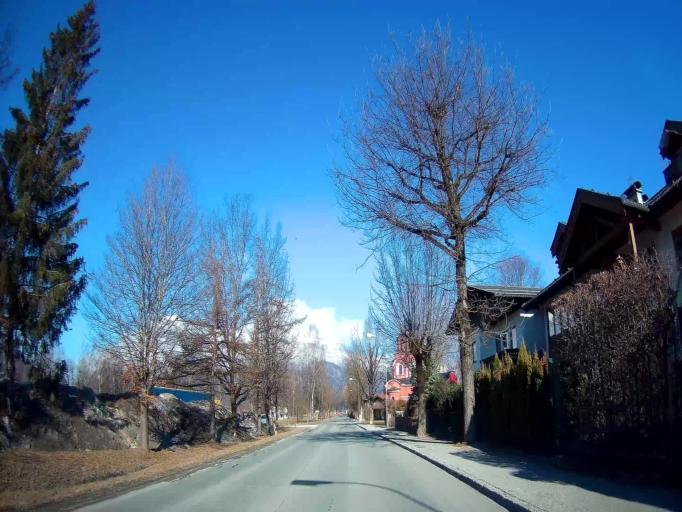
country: AT
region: Salzburg
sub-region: Politischer Bezirk Zell am See
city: Saalfelden am Steinernen Meer
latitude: 47.4318
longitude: 12.8518
